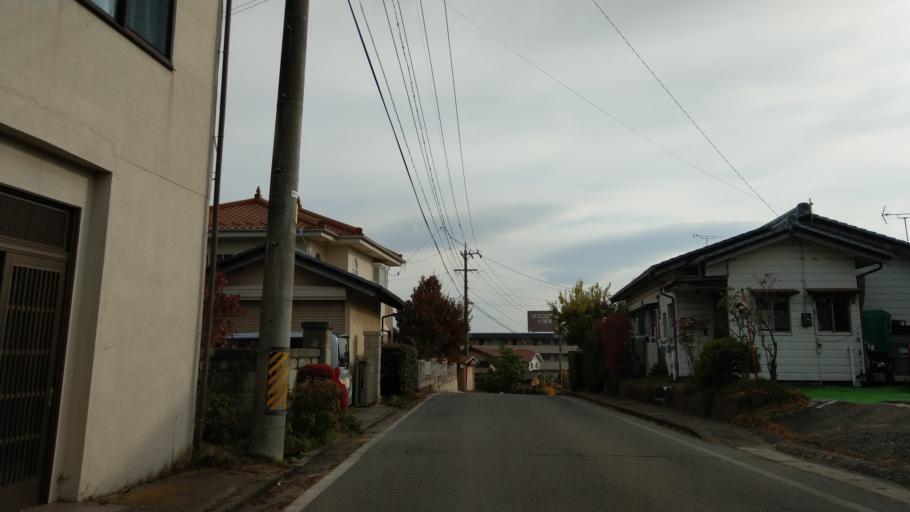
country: JP
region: Nagano
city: Komoro
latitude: 36.3162
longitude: 138.4410
